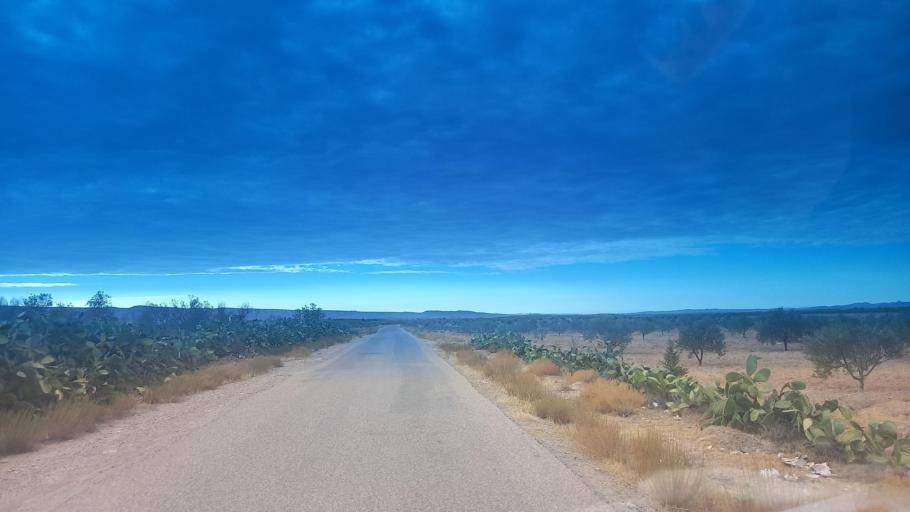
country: TN
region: Al Qasrayn
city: Sbiba
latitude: 35.3879
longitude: 9.0293
